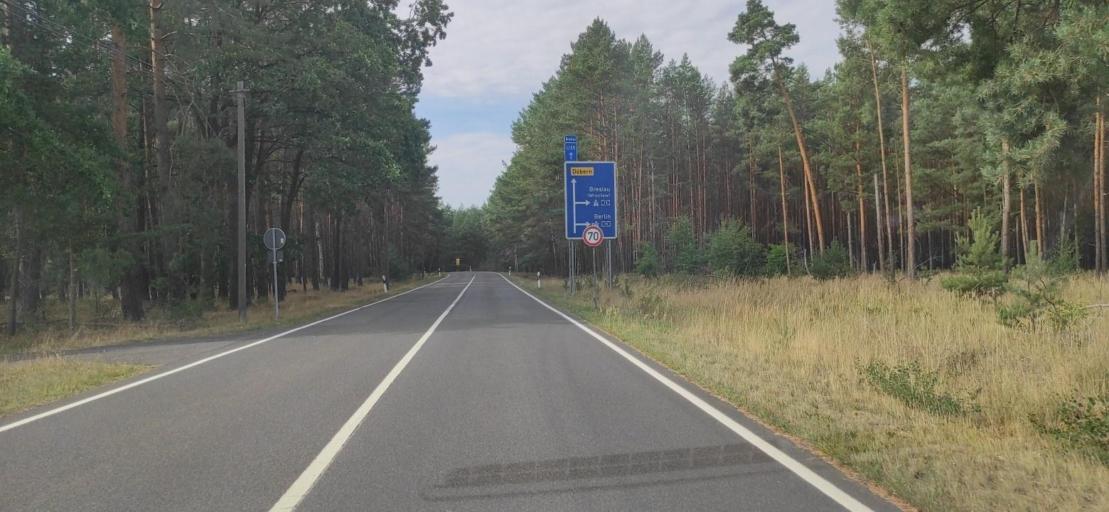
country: PL
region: Lubusz
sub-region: Powiat zarski
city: Trzebiel
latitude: 51.6706
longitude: 14.7378
